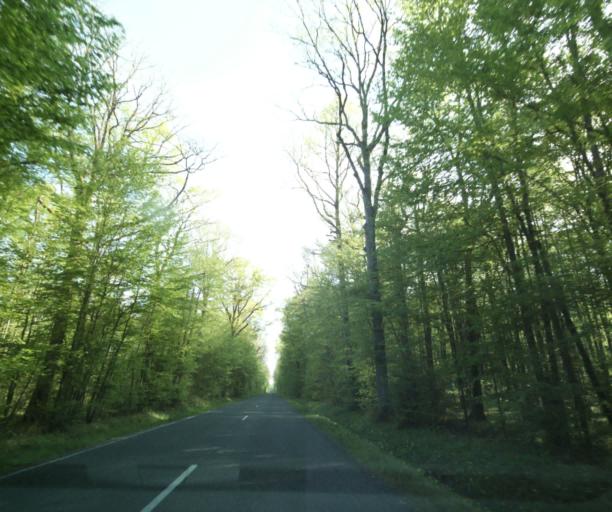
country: FR
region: Ile-de-France
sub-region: Departement de Seine-et-Marne
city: La Chapelle-Gauthier
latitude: 48.5065
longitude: 2.9208
